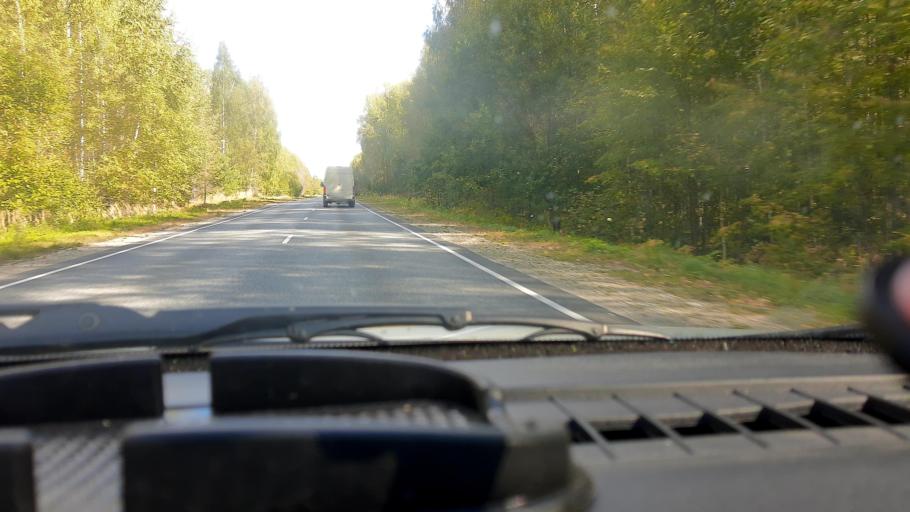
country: RU
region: Kirov
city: Sanchursk
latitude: 56.5761
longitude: 47.1905
